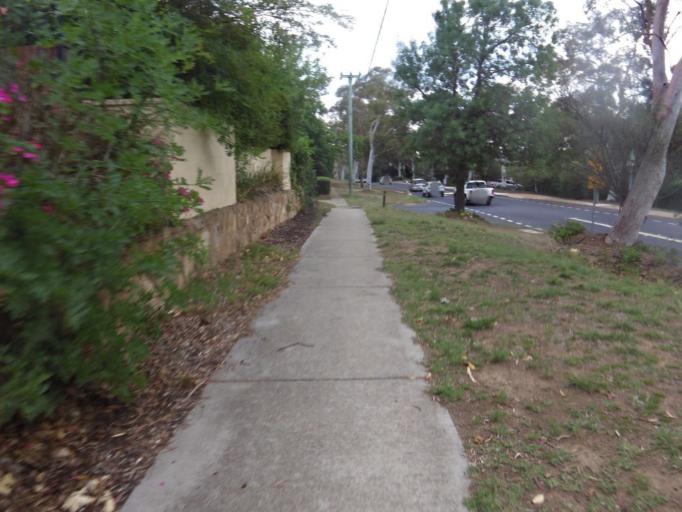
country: AU
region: Australian Capital Territory
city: Forrest
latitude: -35.3414
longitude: 149.1378
